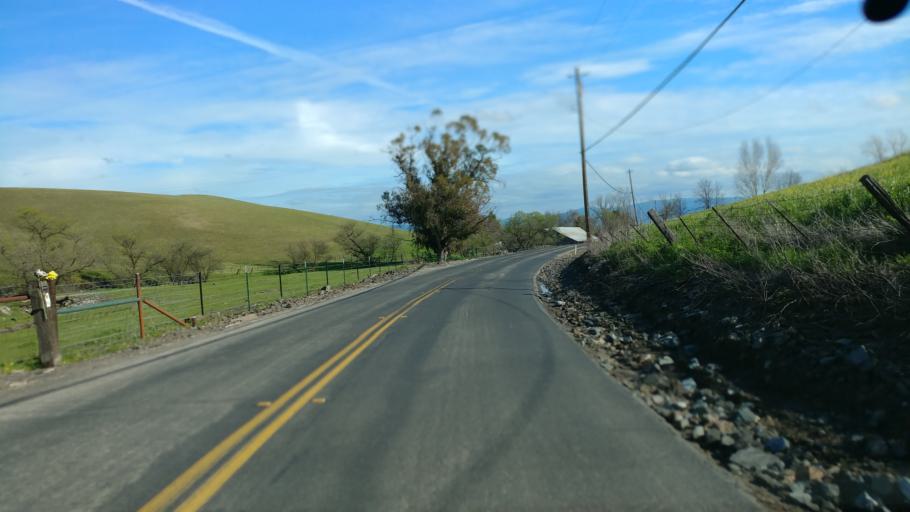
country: US
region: California
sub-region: Alameda County
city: Livermore
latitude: 37.7666
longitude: -121.7965
